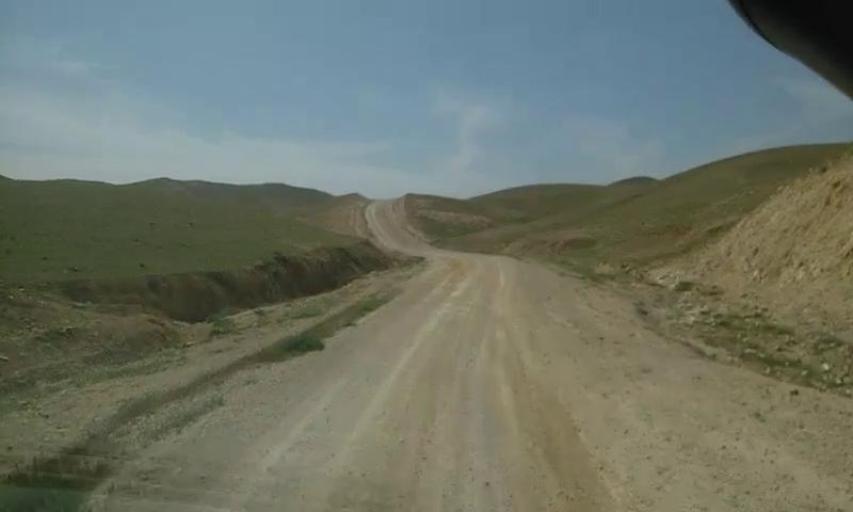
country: PS
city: `Arab ar Rashaydah
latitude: 31.4863
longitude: 35.2822
